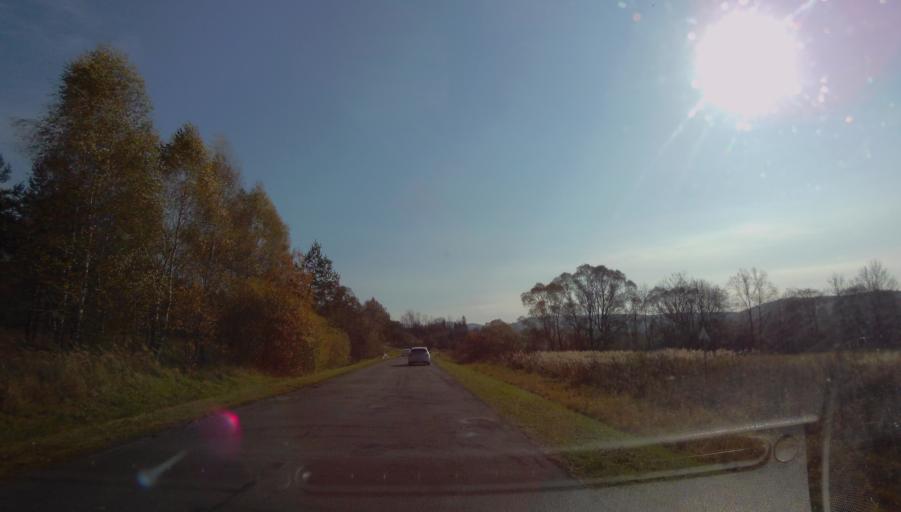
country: PL
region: Subcarpathian Voivodeship
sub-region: Powiat sanocki
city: Komancza
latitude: 49.2402
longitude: 22.1427
